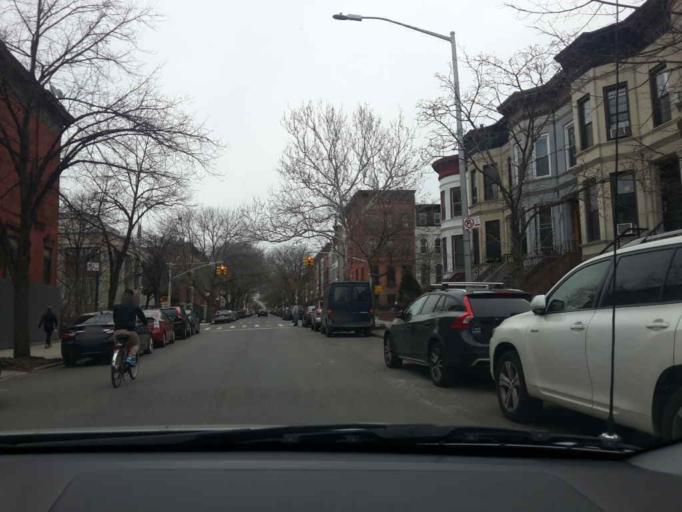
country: US
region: New York
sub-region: Kings County
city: Brooklyn
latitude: 40.6763
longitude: -73.9669
